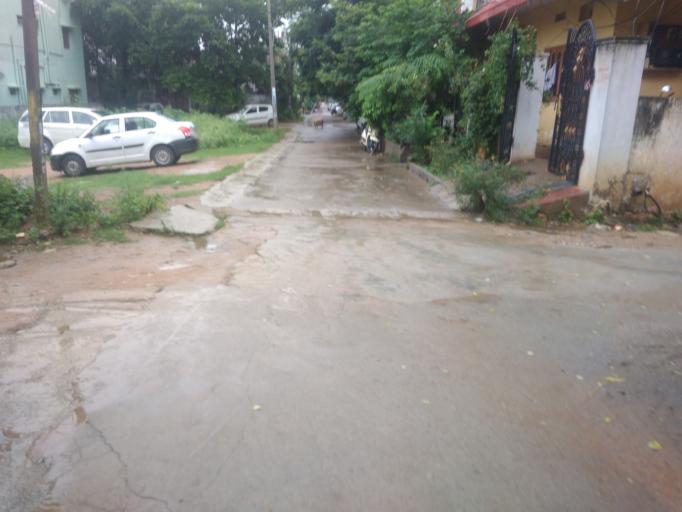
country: IN
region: Telangana
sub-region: Rangareddi
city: Secunderabad
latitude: 17.5149
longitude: 78.5095
